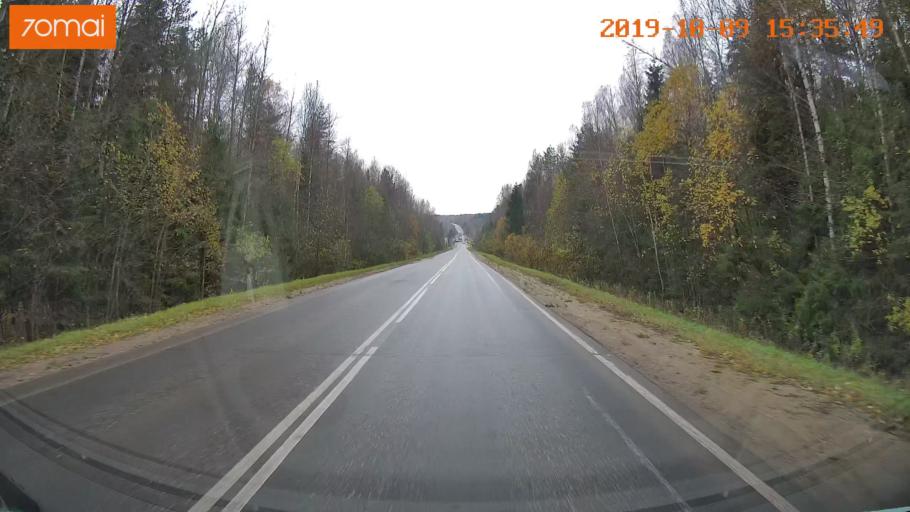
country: RU
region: Kostroma
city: Oktyabr'skiy
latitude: 57.9283
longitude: 41.2197
